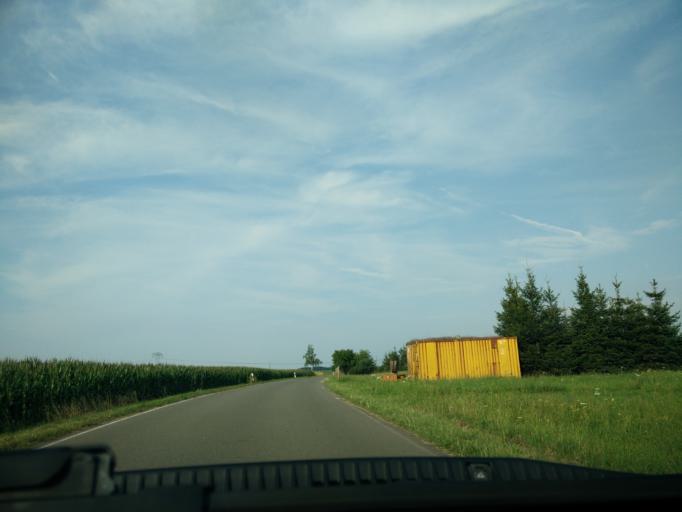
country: DE
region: Saxony
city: Frohburg
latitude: 51.0895
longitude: 12.5623
